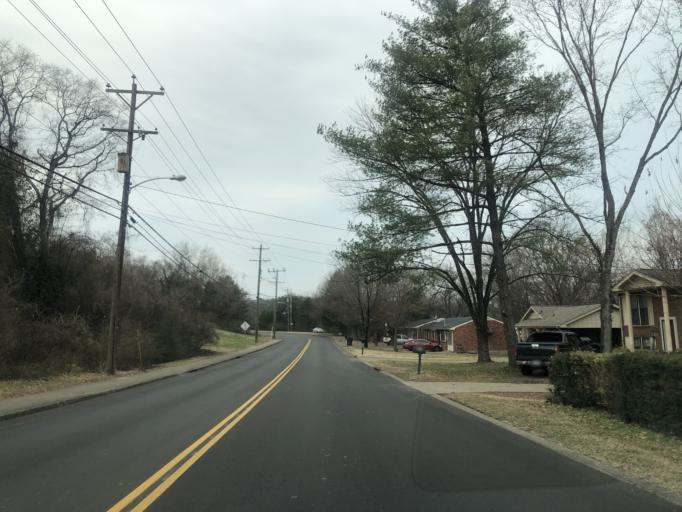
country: US
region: Tennessee
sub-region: Davidson County
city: Oak Hill
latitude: 36.0888
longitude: -86.7174
